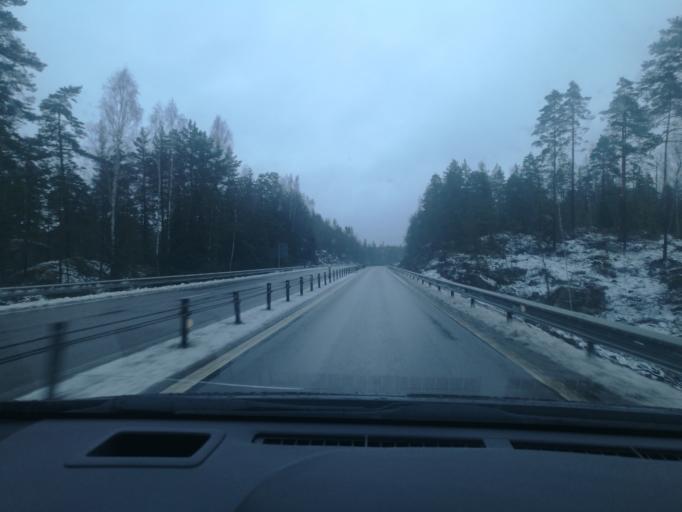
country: SE
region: OEstergoetland
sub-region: Norrkopings Kommun
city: Jursla
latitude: 58.7135
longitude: 16.1629
